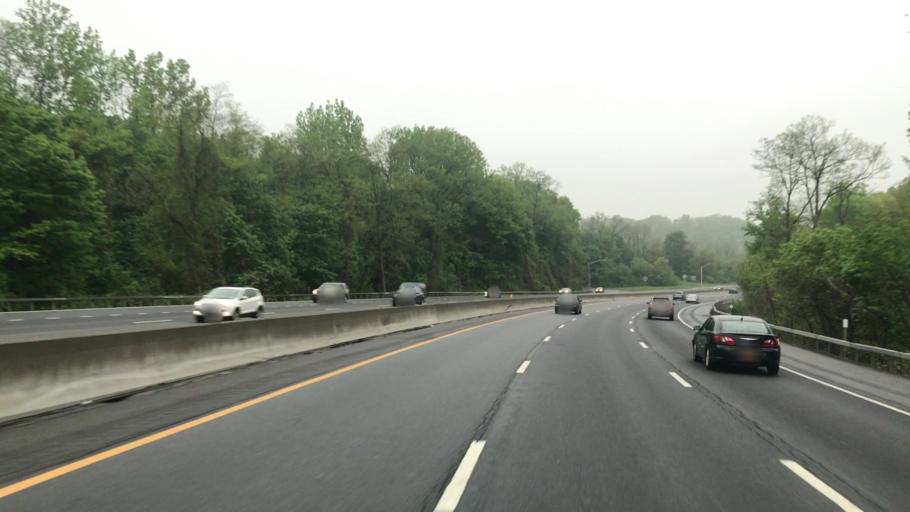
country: US
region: New York
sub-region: Westchester County
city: Bronxville
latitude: 40.9523
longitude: -73.8589
